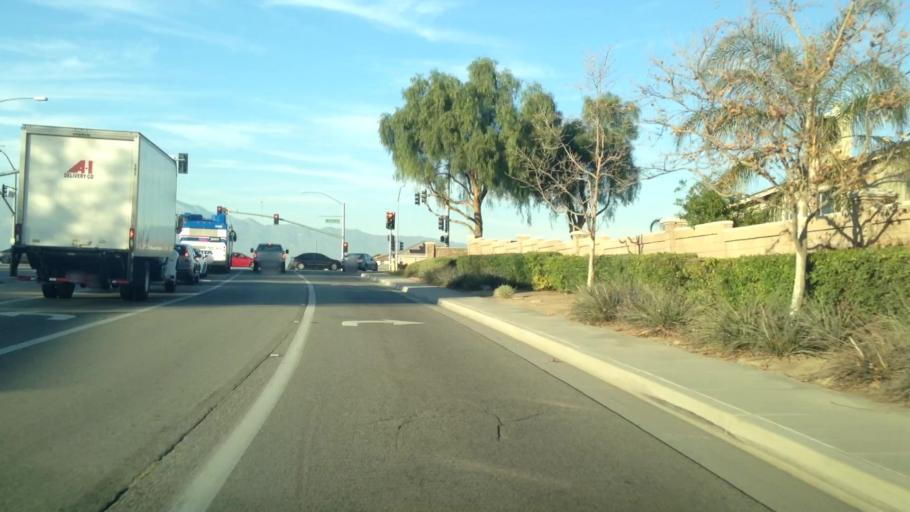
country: US
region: California
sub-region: Riverside County
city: Mira Loma
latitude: 33.9745
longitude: -117.5437
